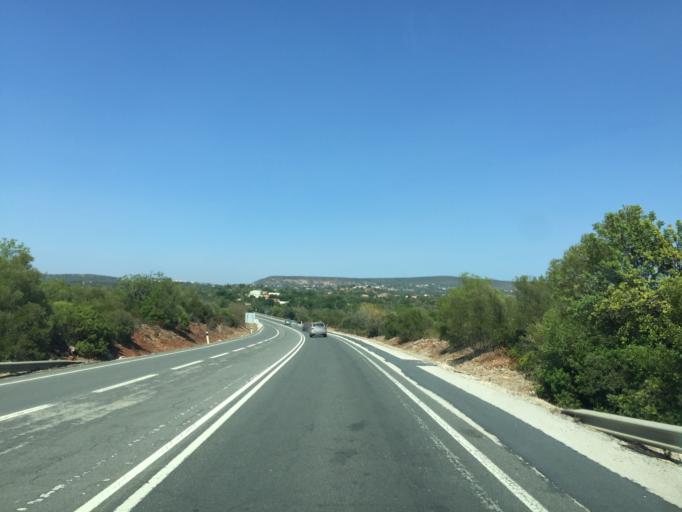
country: PT
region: Faro
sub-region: Silves
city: Sao Bartolomeu de Messines
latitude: 37.2063
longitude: -8.2581
